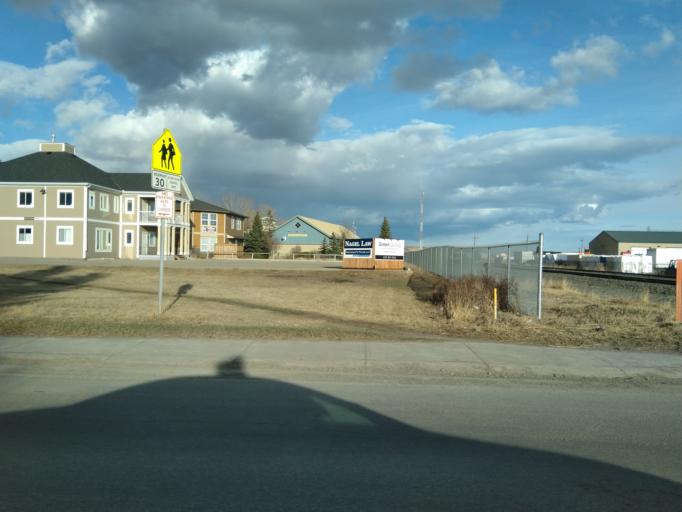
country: CA
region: Alberta
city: Cochrane
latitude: 51.1877
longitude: -114.4637
